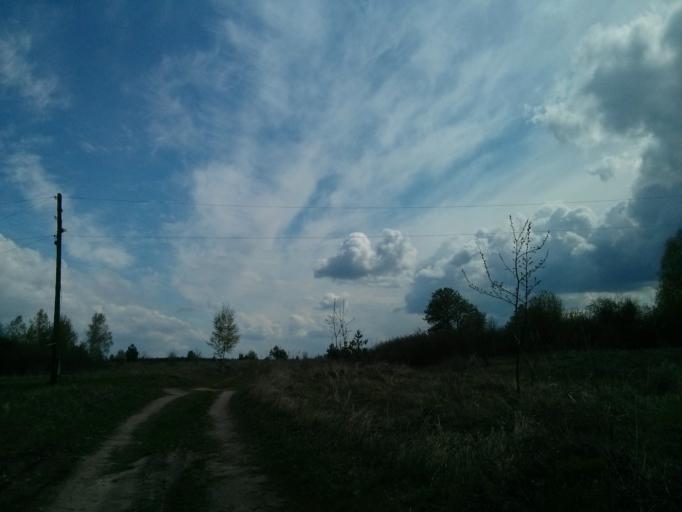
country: RU
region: Nizjnij Novgorod
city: Shimorskoye
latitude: 55.3032
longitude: 41.8463
